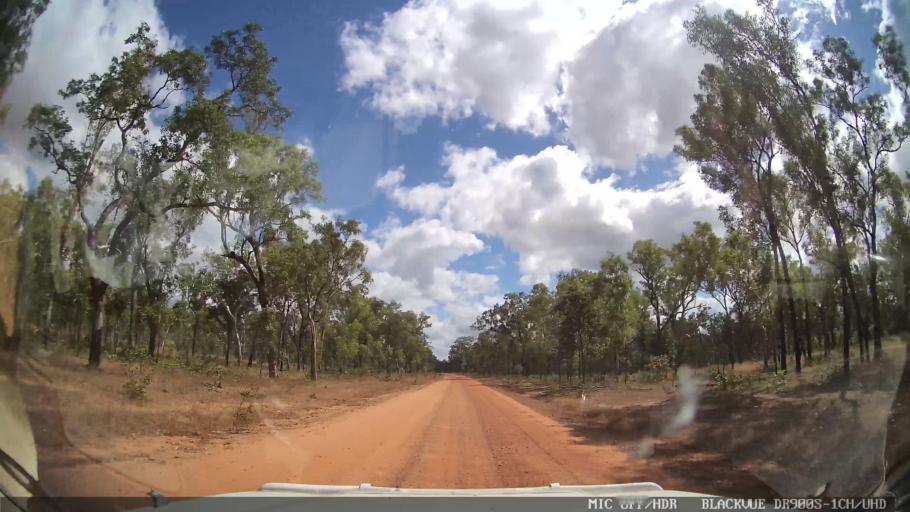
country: AU
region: Queensland
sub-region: Cook
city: Cooktown
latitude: -15.3517
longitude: 144.4650
